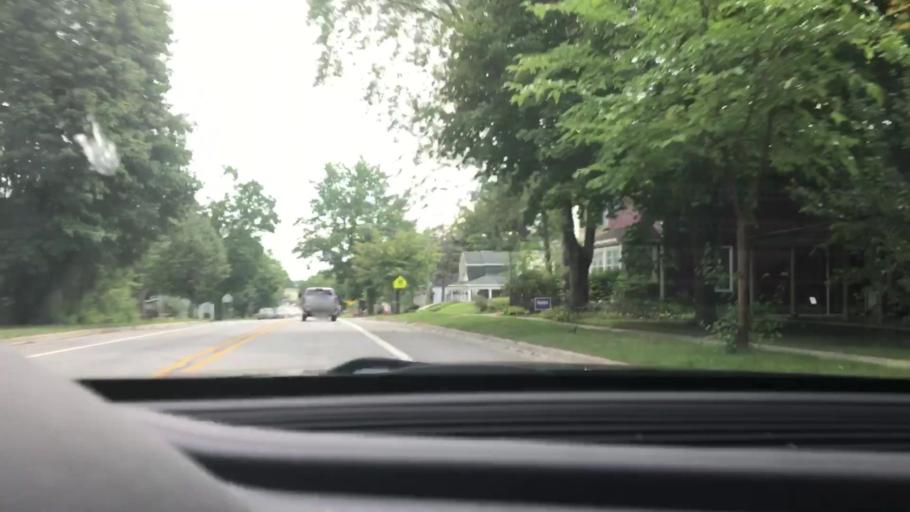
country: US
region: Michigan
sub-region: Antrim County
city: Bellaire
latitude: 44.9821
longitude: -85.2103
